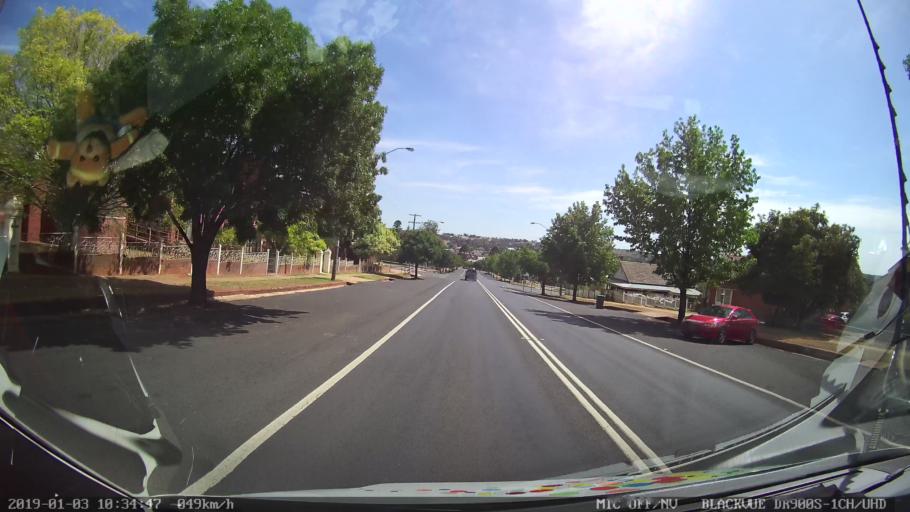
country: AU
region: New South Wales
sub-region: Young
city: Young
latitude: -34.3195
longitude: 148.2922
